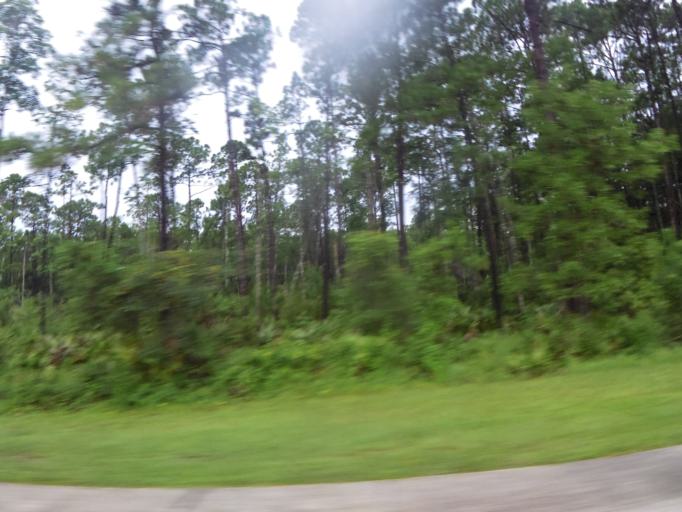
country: US
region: Florida
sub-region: Duval County
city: Jacksonville Beach
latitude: 30.2699
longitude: -81.5103
